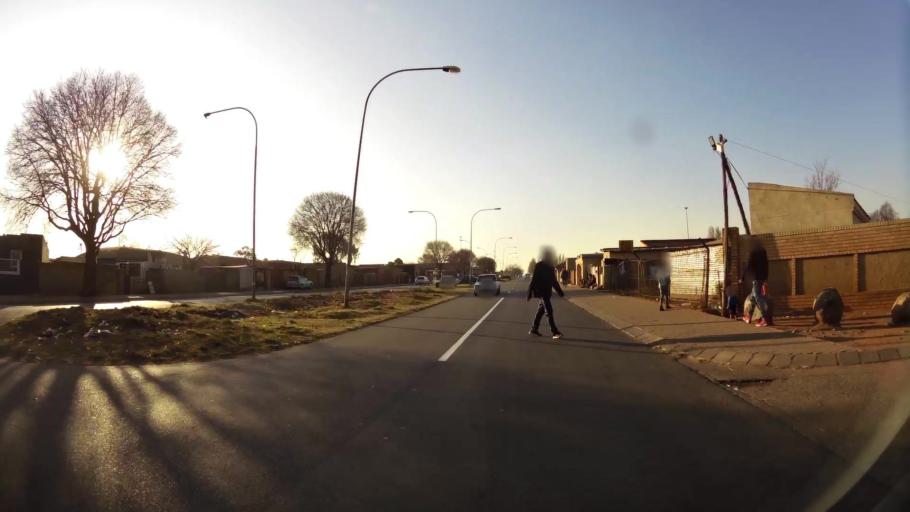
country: ZA
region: Gauteng
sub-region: City of Johannesburg Metropolitan Municipality
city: Soweto
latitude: -26.2562
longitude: 27.8778
